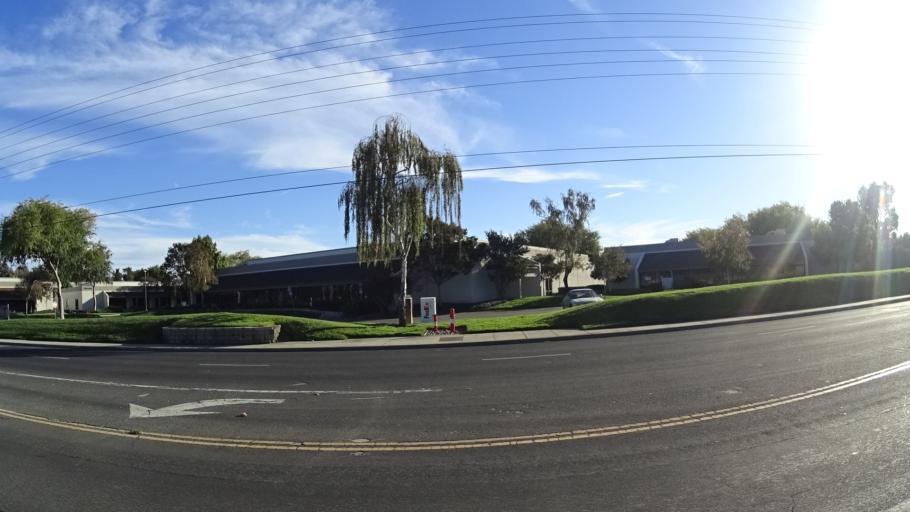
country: US
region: California
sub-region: Santa Clara County
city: Santa Clara
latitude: 37.3695
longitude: -121.9679
